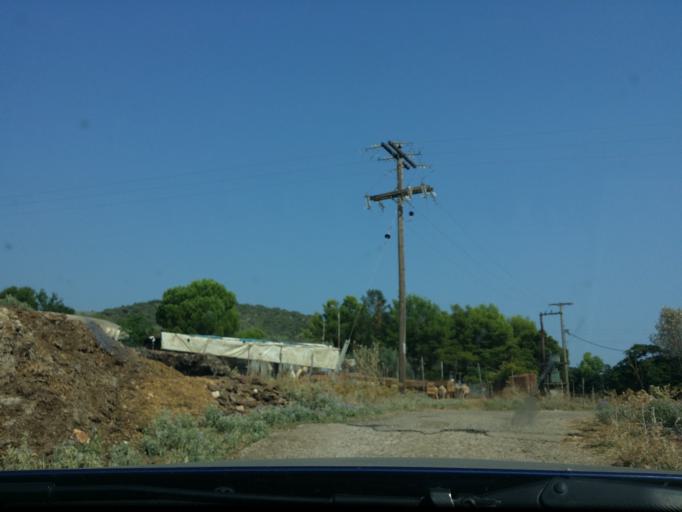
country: GR
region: West Greece
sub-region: Nomos Aitolias kai Akarnanias
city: Stanos
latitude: 38.8258
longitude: 21.1706
